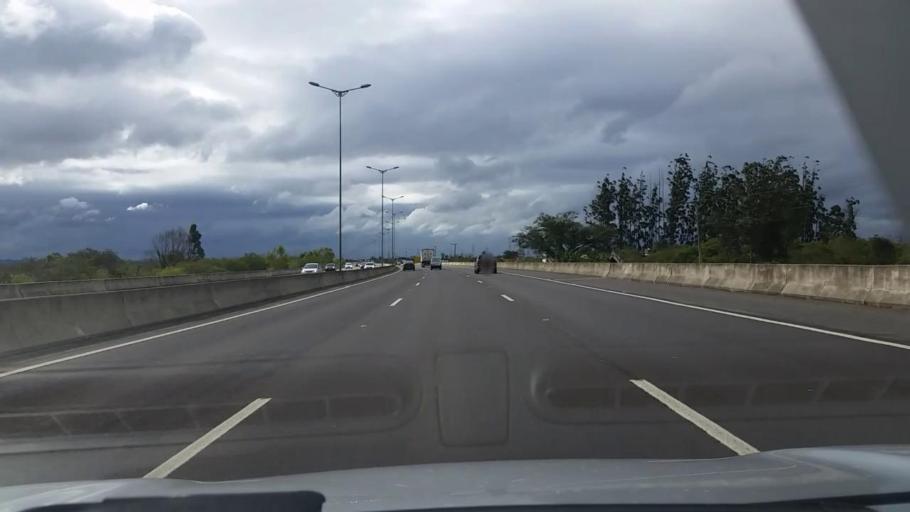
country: BR
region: Rio Grande do Sul
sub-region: Canoas
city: Canoas
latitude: -29.9573
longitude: -51.2023
